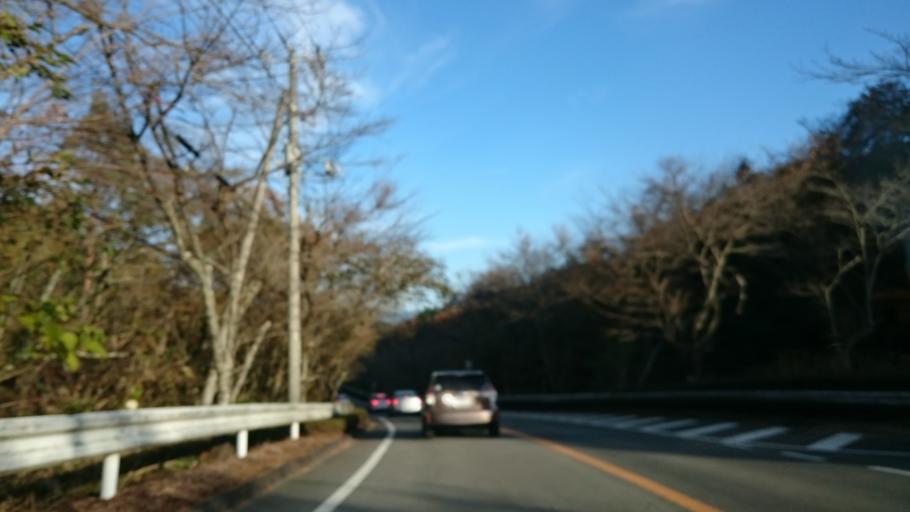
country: JP
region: Shizuoka
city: Heda
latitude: 34.9764
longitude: 138.9155
